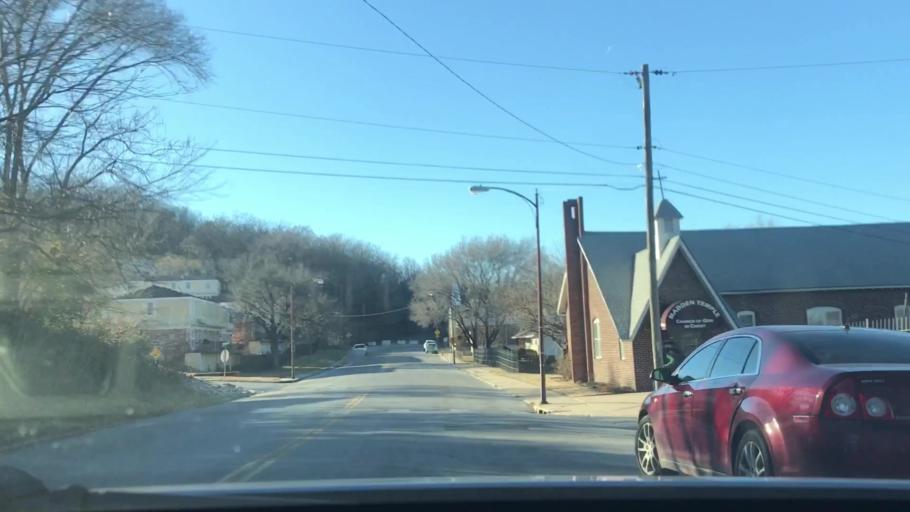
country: US
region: Kansas
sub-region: Johnson County
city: Roeland Park
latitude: 39.0716
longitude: -94.6549
